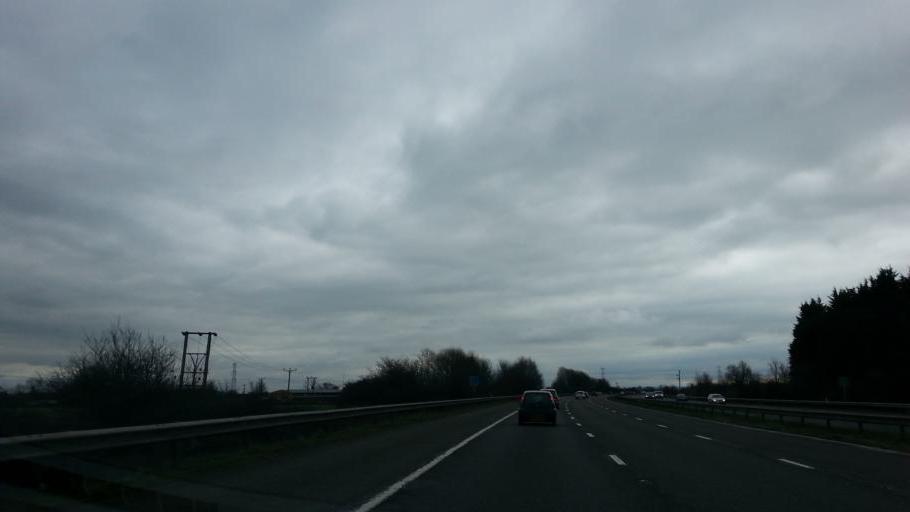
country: GB
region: England
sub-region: Somerset
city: Puriton
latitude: 51.1389
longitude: -2.9699
